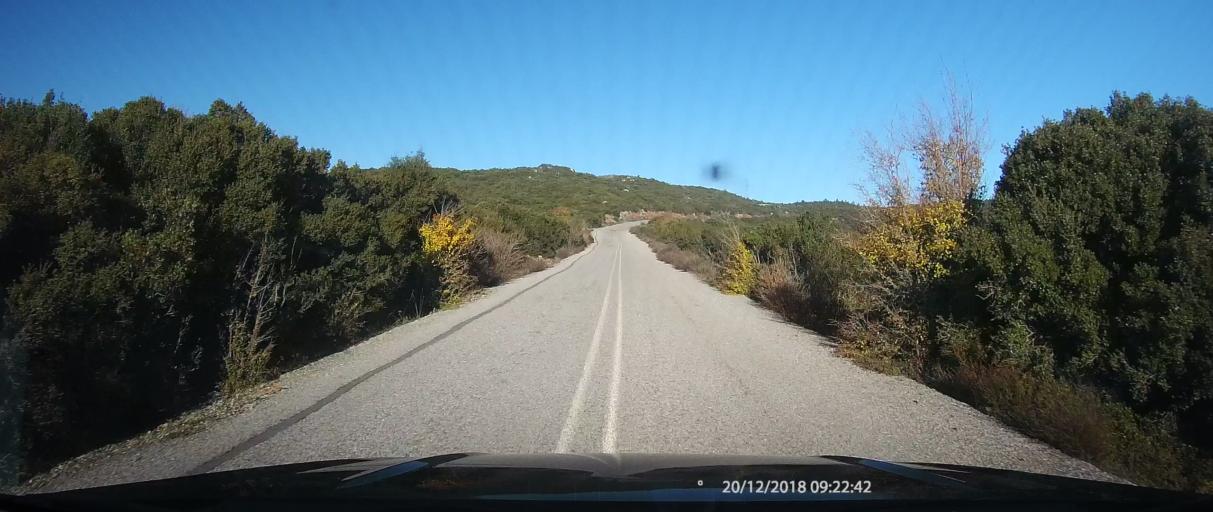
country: GR
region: Peloponnese
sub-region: Nomos Lakonias
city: Molaoi
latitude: 36.9514
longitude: 22.9014
